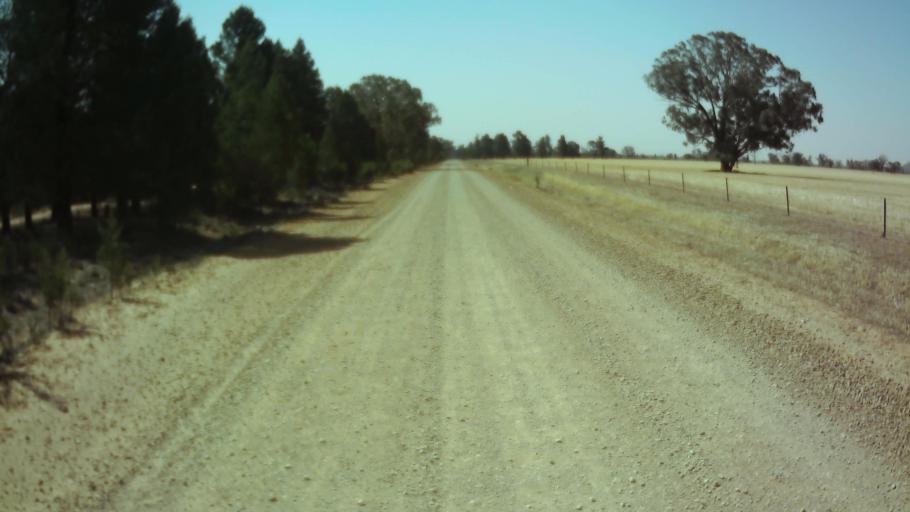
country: AU
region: New South Wales
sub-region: Weddin
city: Grenfell
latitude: -33.9572
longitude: 147.9318
